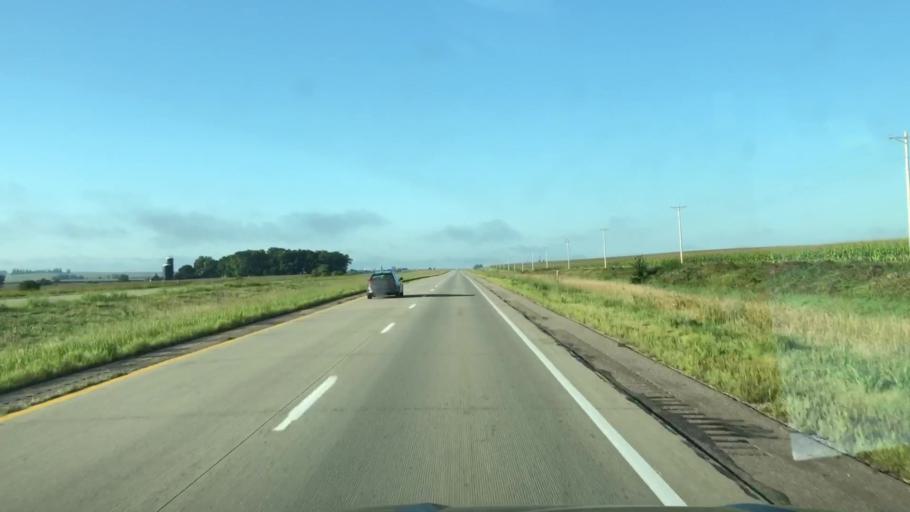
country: US
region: Iowa
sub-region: Sioux County
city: Alton
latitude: 42.9487
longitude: -96.0377
